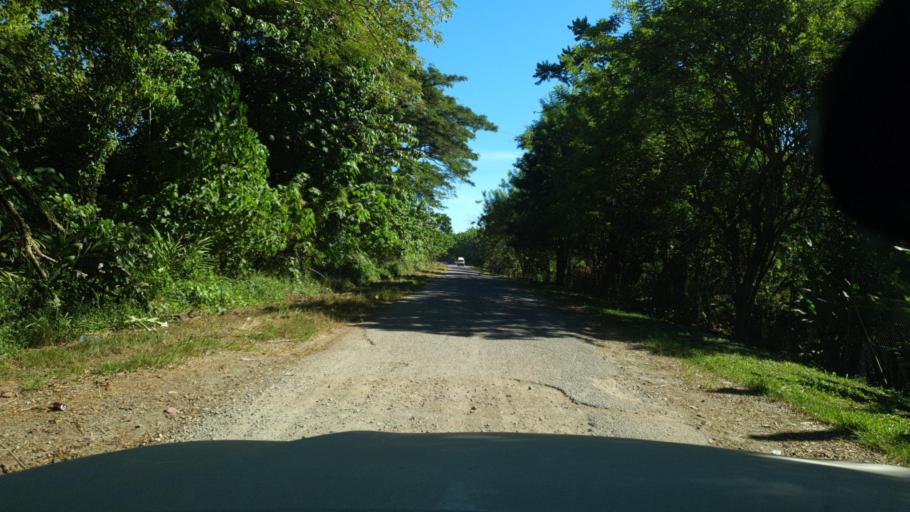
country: SB
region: Guadalcanal
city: Honiara
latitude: -9.3323
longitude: 159.8143
